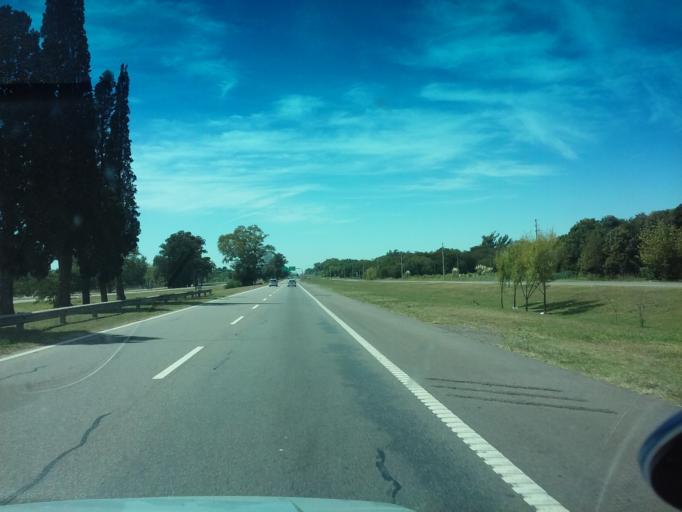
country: AR
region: Buenos Aires
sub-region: Partido de Mercedes
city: Mercedes
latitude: -34.6597
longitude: -59.3720
